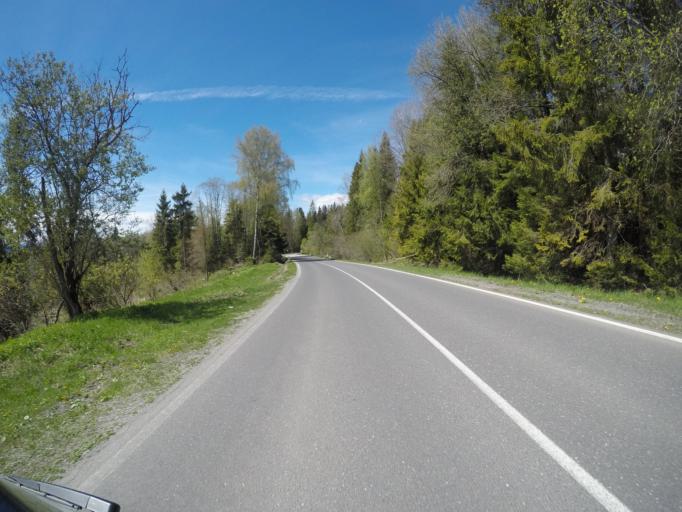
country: SK
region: Presovsky
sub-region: Okres Poprad
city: Strba
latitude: 49.0973
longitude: 20.0669
